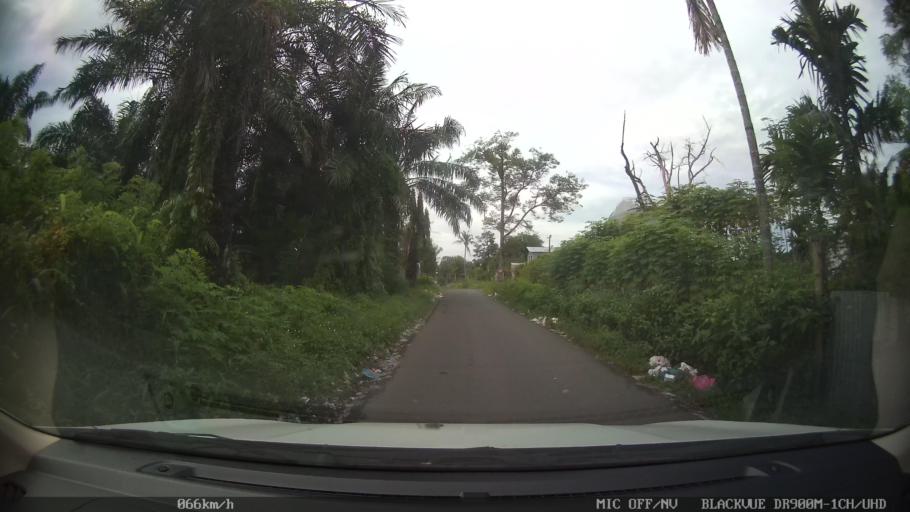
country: ID
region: North Sumatra
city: Sunggal
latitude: 3.5733
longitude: 98.5775
